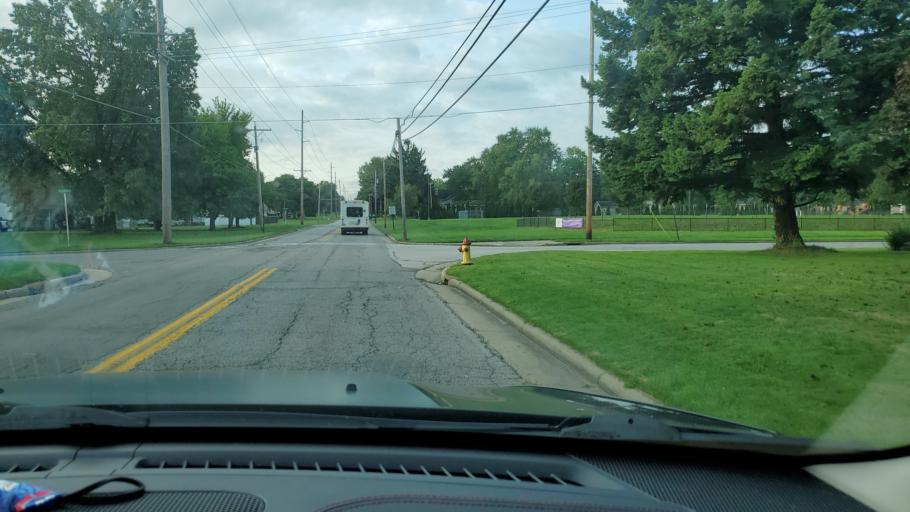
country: US
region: Ohio
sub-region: Mahoning County
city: Struthers
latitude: 41.0487
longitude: -80.6216
